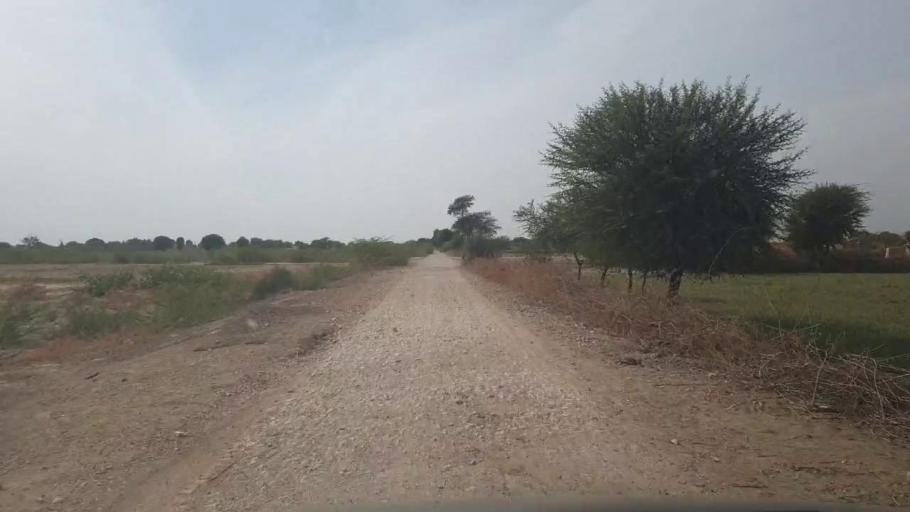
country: PK
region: Sindh
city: Kunri
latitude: 25.2382
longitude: 69.5973
